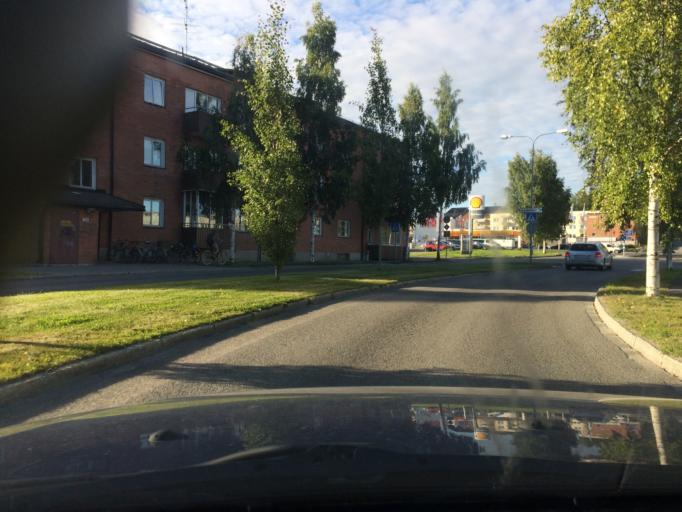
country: SE
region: Norrbotten
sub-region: Pitea Kommun
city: Pitea
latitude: 65.3194
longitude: 21.4729
